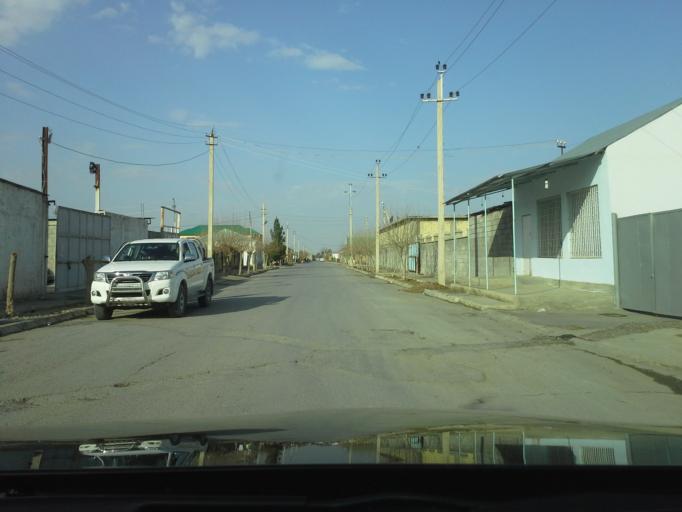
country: TM
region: Ahal
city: Abadan
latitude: 38.0198
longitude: 58.2313
